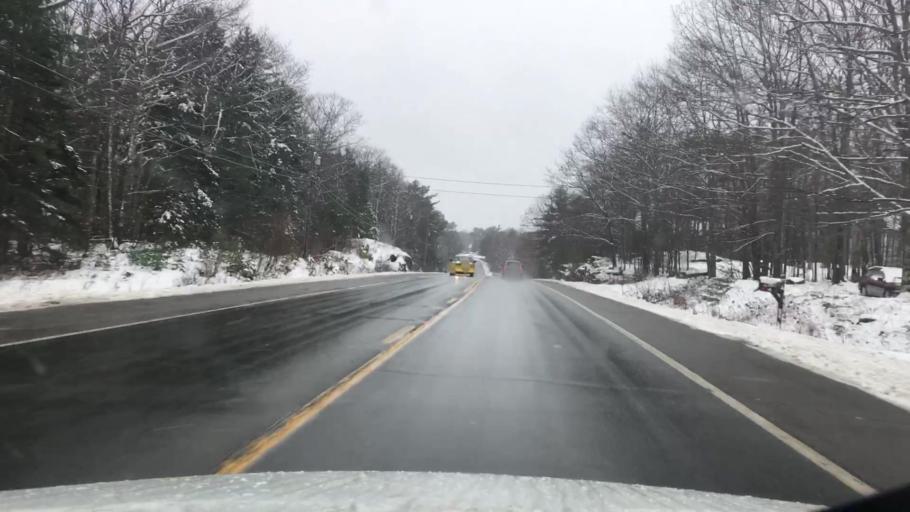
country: US
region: Maine
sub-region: Knox County
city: Rockland
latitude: 44.1658
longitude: -69.1673
